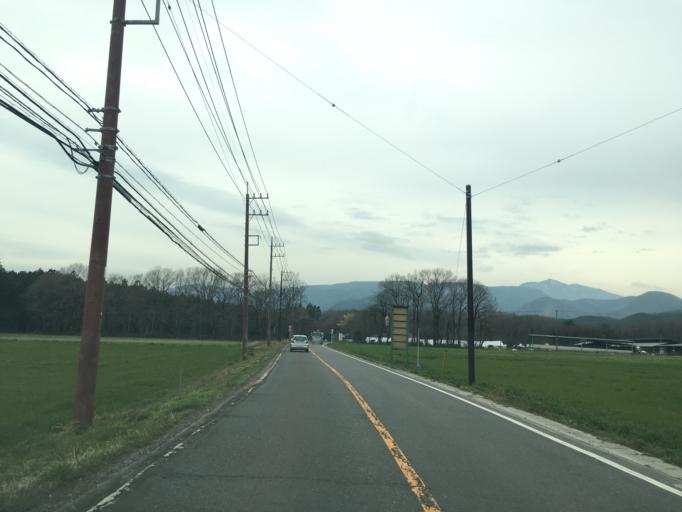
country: JP
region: Tochigi
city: Kuroiso
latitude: 36.9613
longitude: 139.9110
